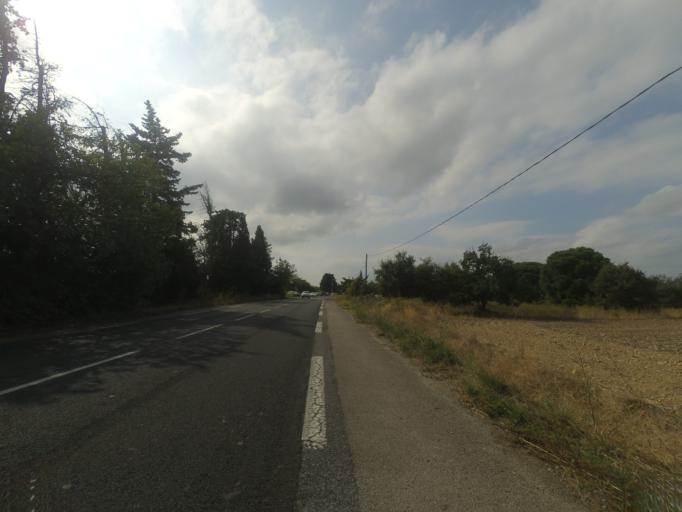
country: FR
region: Languedoc-Roussillon
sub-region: Departement des Pyrenees-Orientales
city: Villeneuve-la-Riviere
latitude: 42.6793
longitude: 2.8132
